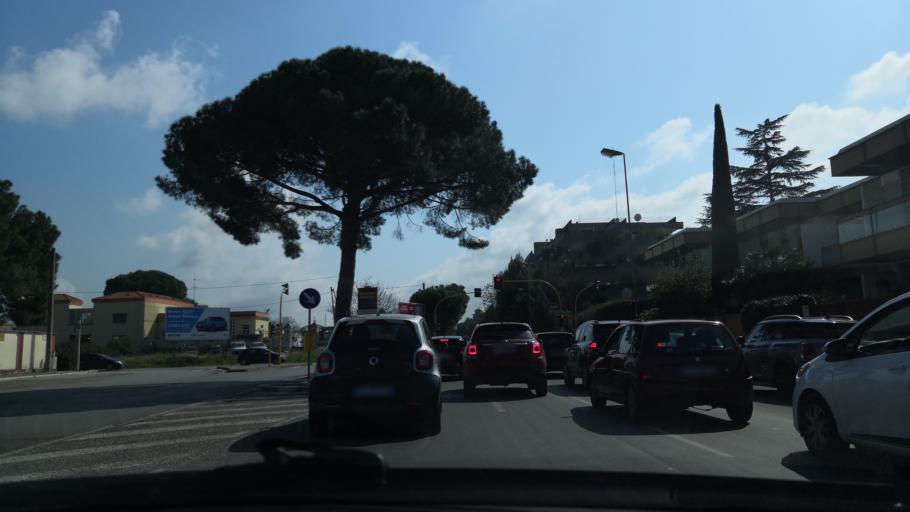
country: IT
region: Apulia
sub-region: Provincia di Bari
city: Bari
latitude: 41.0964
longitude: 16.8736
